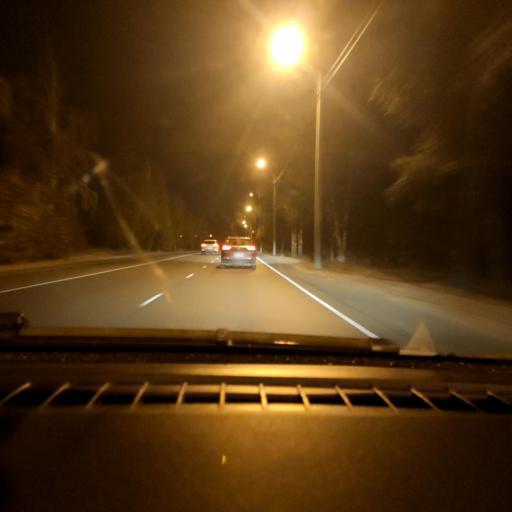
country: RU
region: Voronezj
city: Voronezh
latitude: 51.6774
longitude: 39.2734
